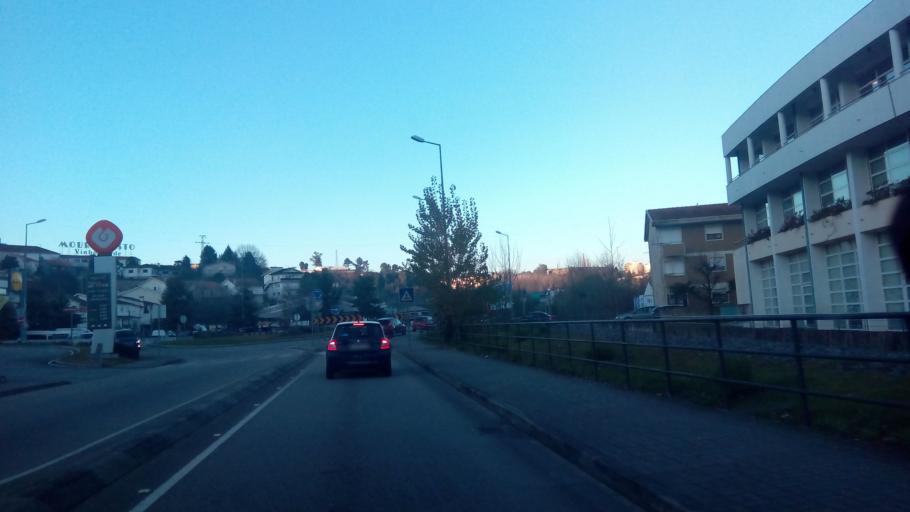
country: PT
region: Porto
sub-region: Amarante
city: Amarante
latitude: 41.2722
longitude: -8.0891
